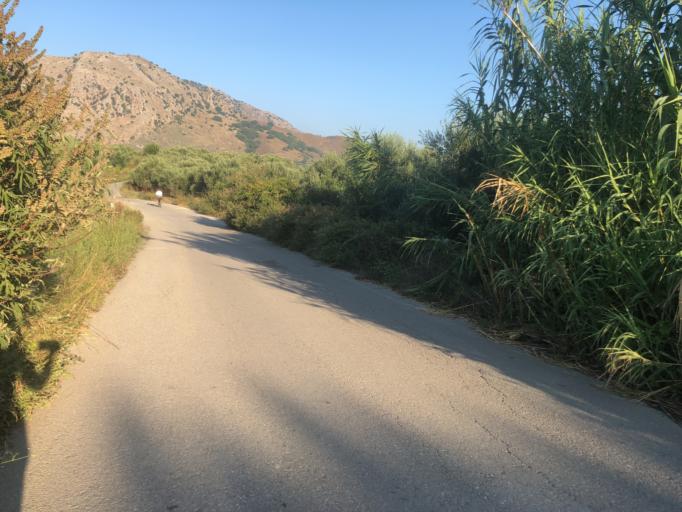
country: GR
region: Crete
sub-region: Nomos Chanias
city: Georgioupolis
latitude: 35.3382
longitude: 24.2882
